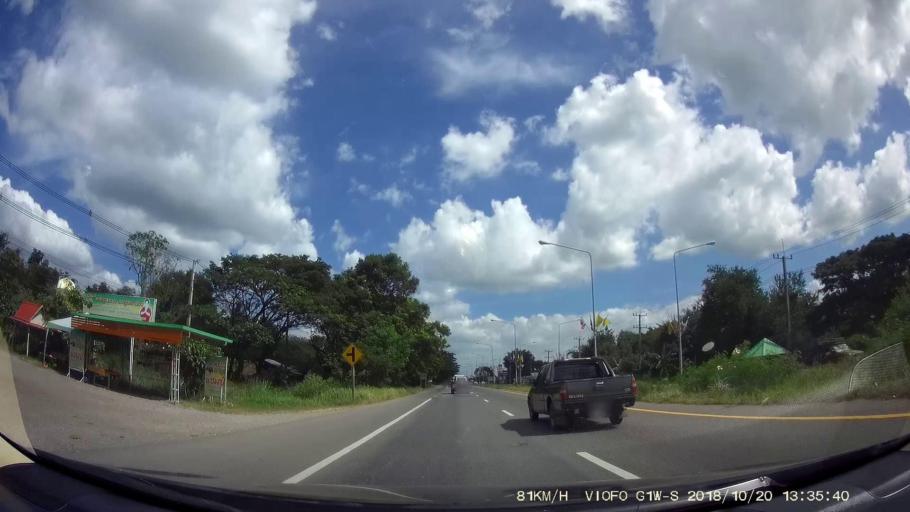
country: TH
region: Khon Kaen
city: Chum Phae
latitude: 16.5674
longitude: 102.0492
